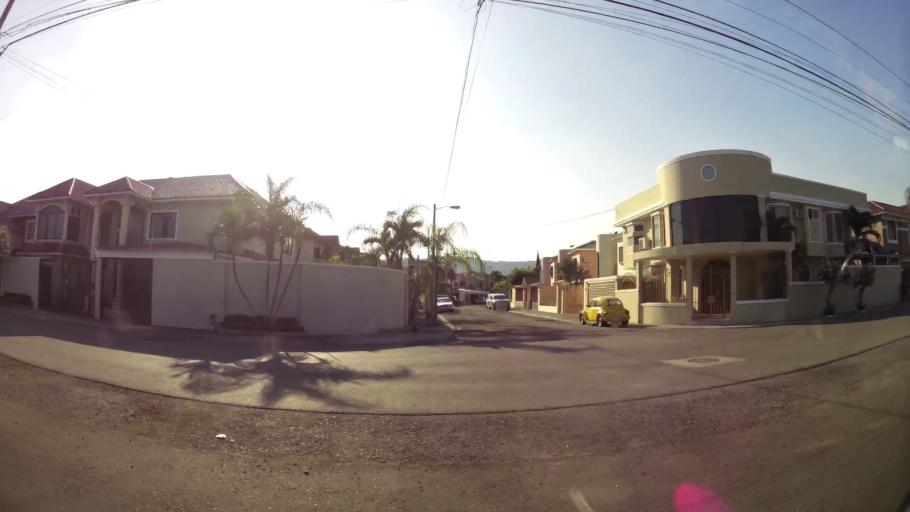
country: EC
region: Guayas
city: Santa Lucia
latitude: -2.1948
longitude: -79.9692
